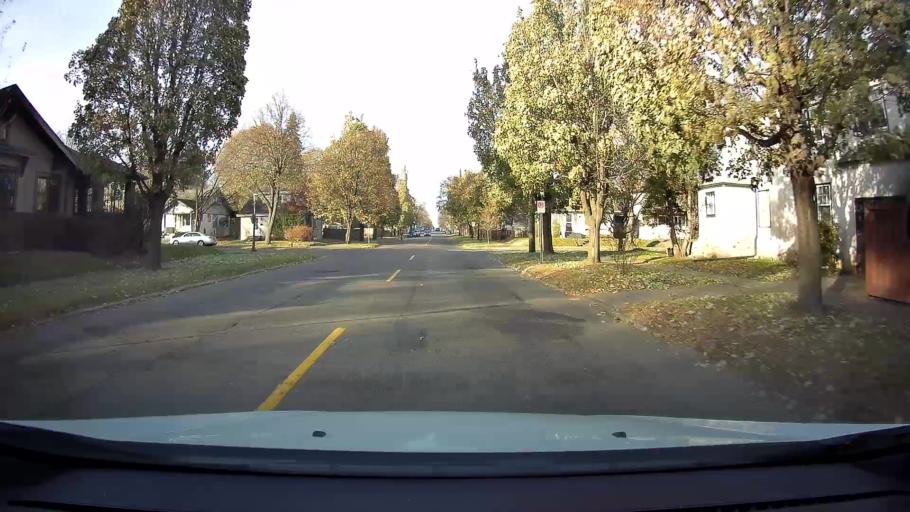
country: US
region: Minnesota
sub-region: Ramsey County
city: Falcon Heights
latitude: 44.9375
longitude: -93.1569
